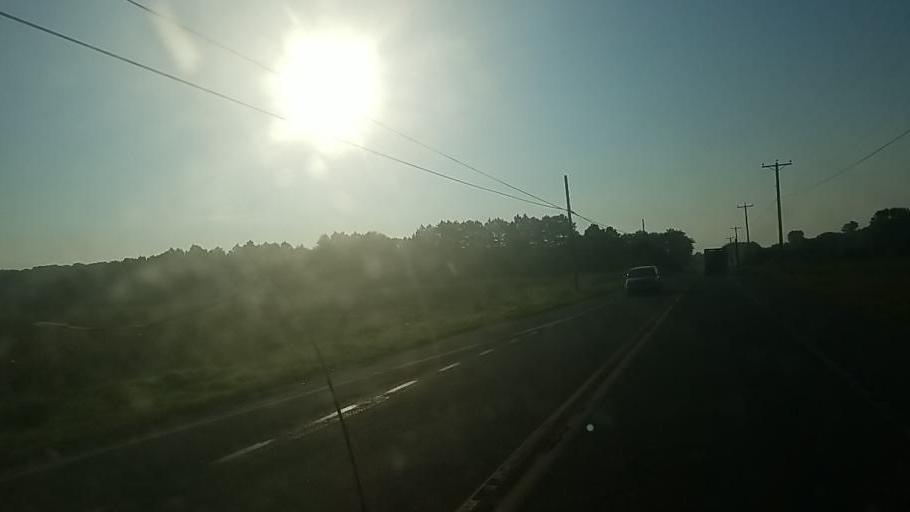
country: US
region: Maryland
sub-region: Worcester County
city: Ocean Pines
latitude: 38.4632
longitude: -75.1447
